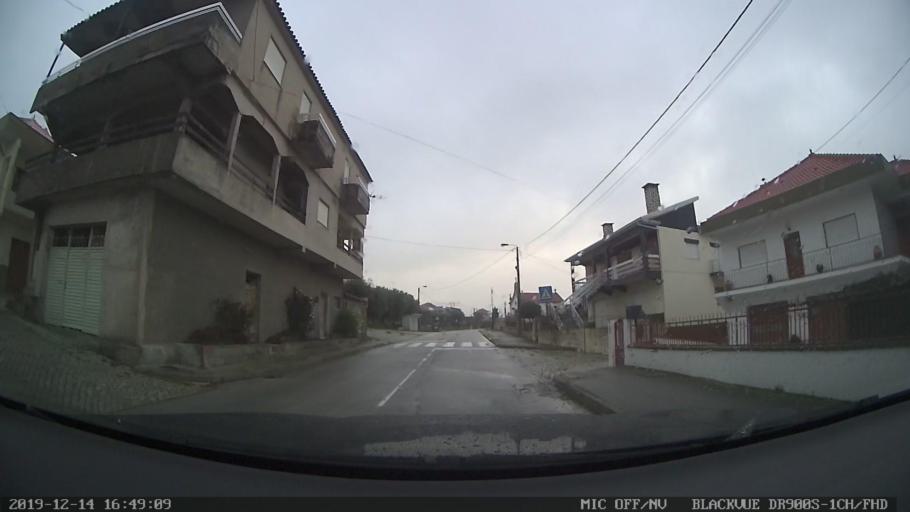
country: PT
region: Vila Real
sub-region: Murca
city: Murca
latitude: 41.4075
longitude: -7.5024
